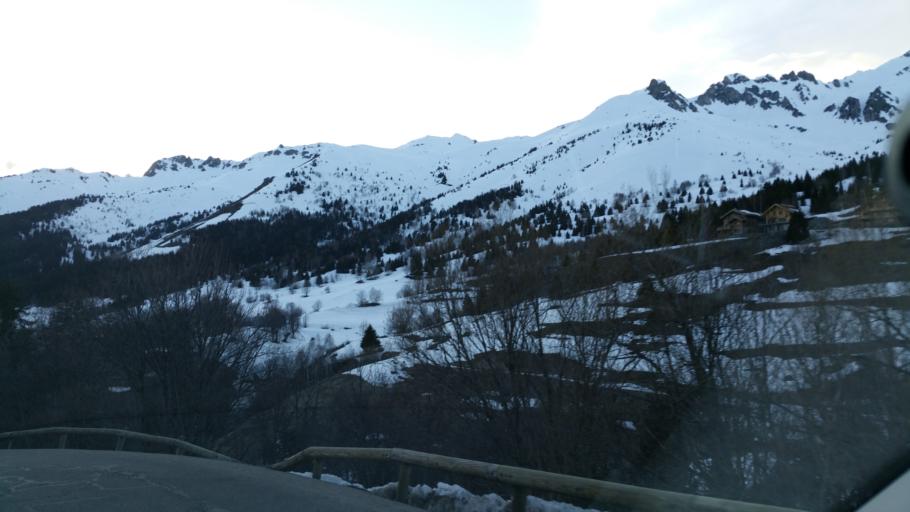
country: FR
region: Rhone-Alpes
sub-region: Departement de la Savoie
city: La Chambre
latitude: 45.4174
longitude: 6.3604
